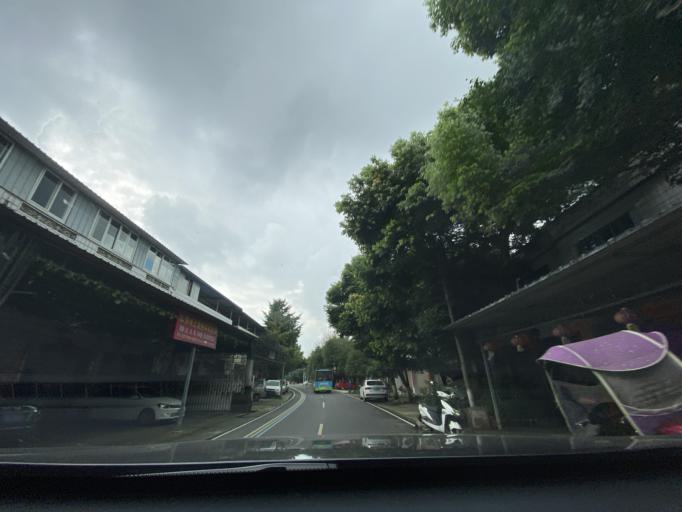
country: CN
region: Sichuan
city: Wujin
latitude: 30.4082
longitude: 103.9909
